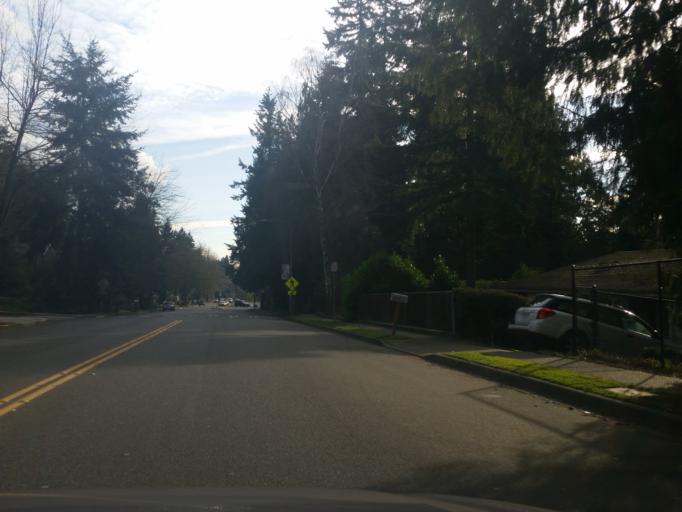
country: US
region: Washington
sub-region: King County
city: Shoreline
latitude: 47.7370
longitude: -122.3237
